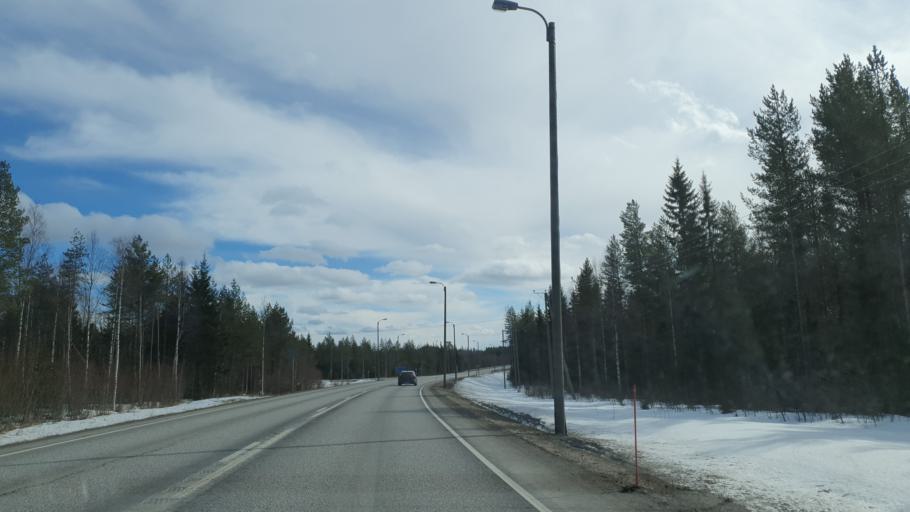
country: FI
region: Kainuu
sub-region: Kajaani
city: Paltamo
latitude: 64.3814
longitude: 28.0190
